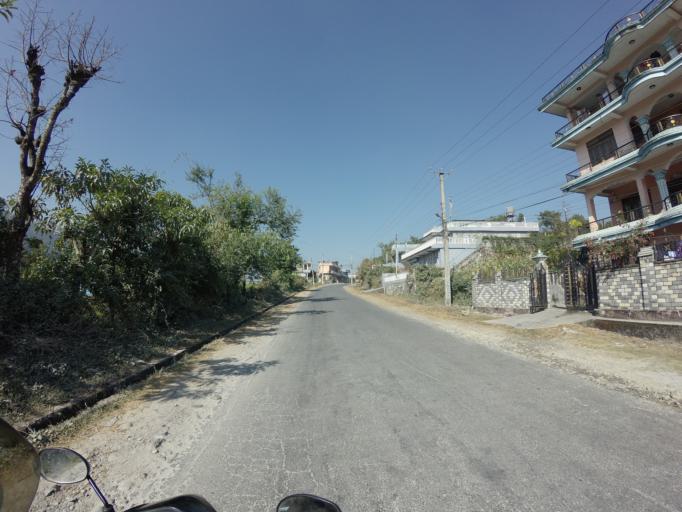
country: NP
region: Western Region
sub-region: Gandaki Zone
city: Pokhara
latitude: 28.2537
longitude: 83.9839
